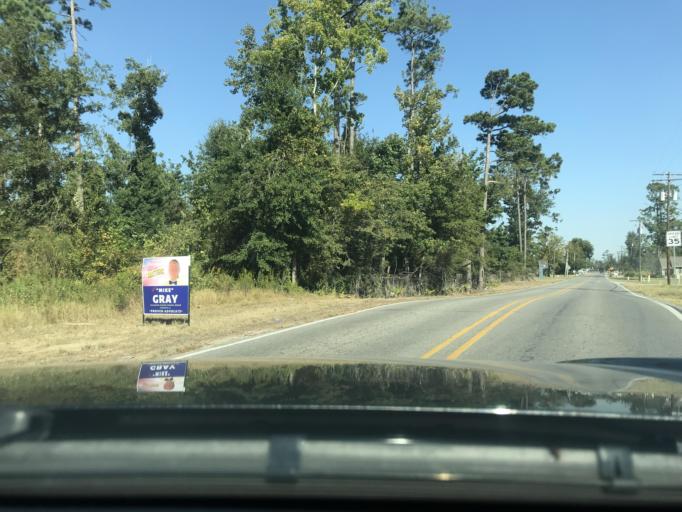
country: US
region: Louisiana
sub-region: Calcasieu Parish
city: Moss Bluff
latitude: 30.3116
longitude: -93.2000
